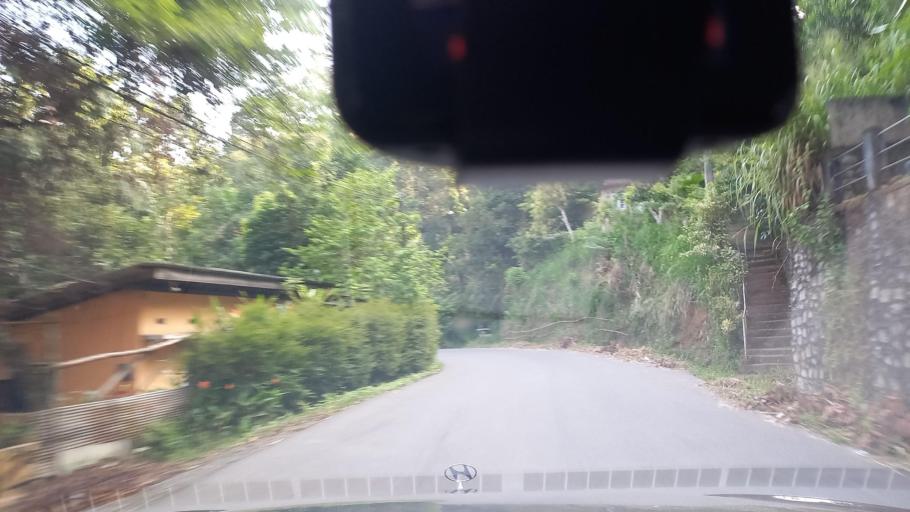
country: LK
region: Central
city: Gampola
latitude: 7.2287
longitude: 80.6036
